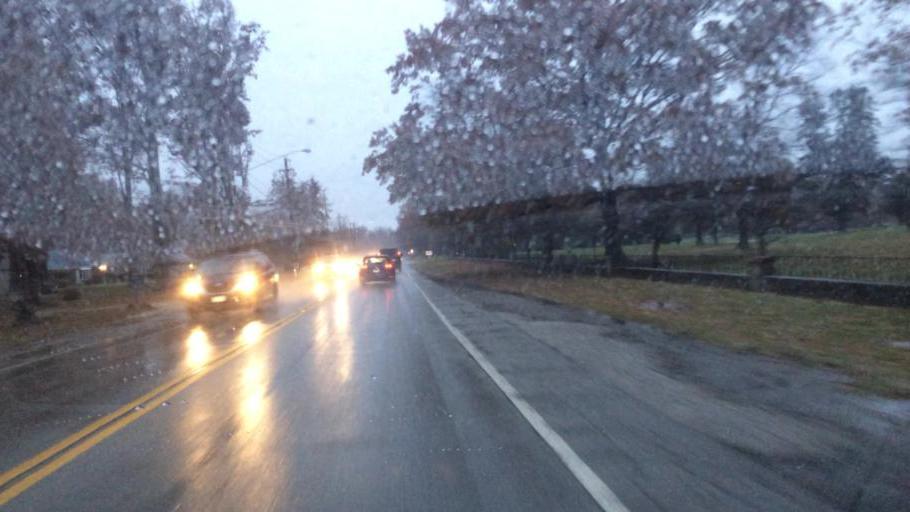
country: US
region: Ohio
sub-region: Cuyahoga County
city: Olmsted Falls
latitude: 41.3974
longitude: -81.9039
